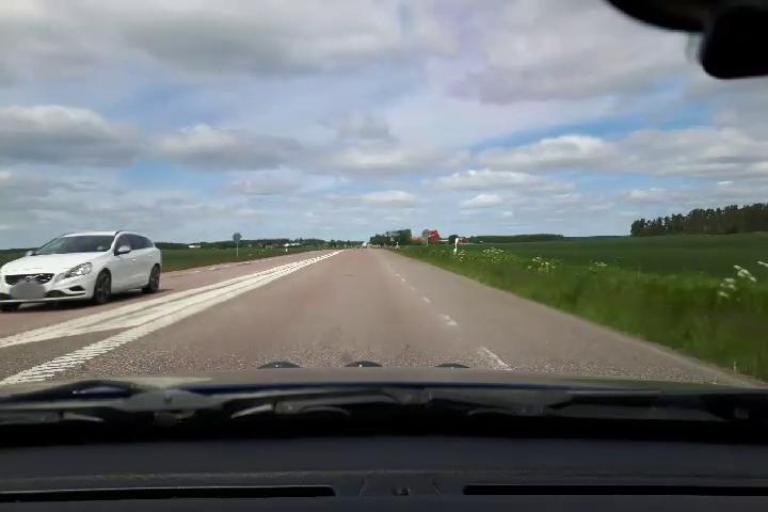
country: SE
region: Uppsala
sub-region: Uppsala Kommun
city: Gamla Uppsala
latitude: 59.9130
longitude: 17.6063
